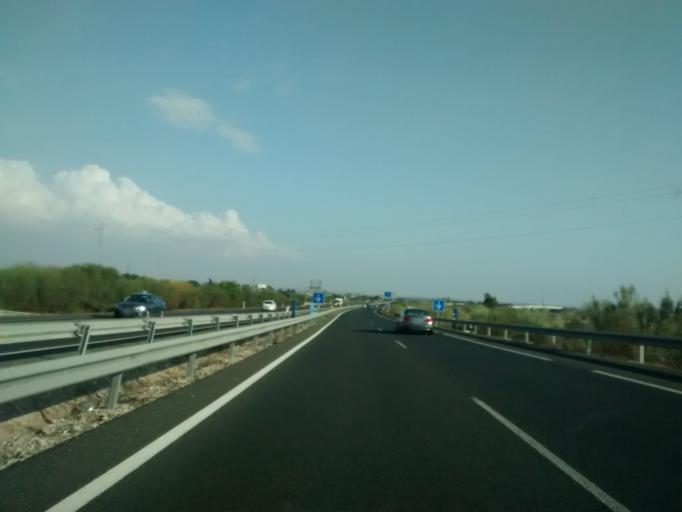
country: ES
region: Andalusia
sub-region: Provincia de Cadiz
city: Puerto Real
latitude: 36.5273
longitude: -6.1666
